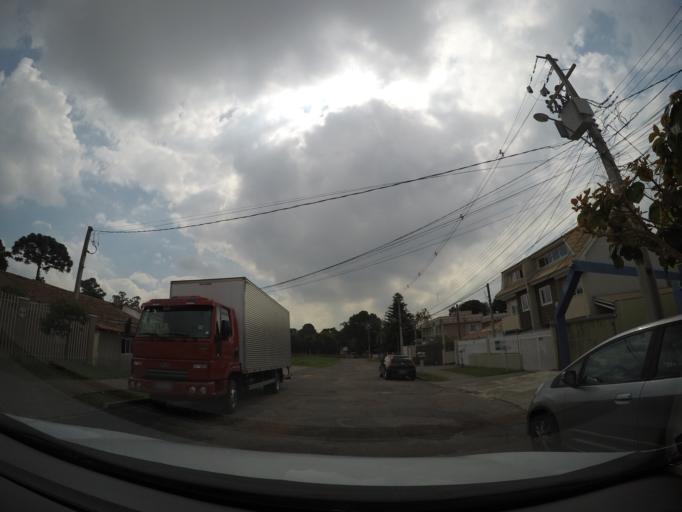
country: BR
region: Parana
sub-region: Sao Jose Dos Pinhais
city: Sao Jose dos Pinhais
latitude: -25.4998
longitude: -49.2424
